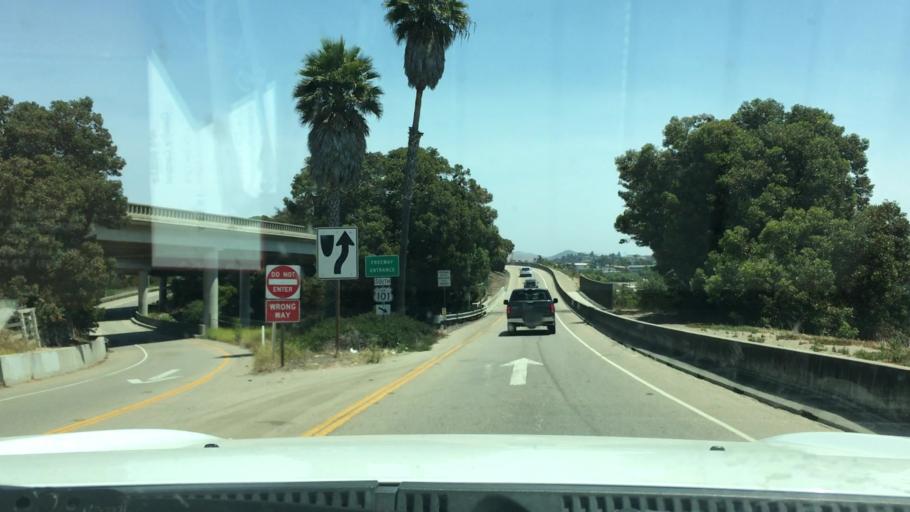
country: US
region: California
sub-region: San Luis Obispo County
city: Pismo Beach
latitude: 35.1396
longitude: -120.6372
